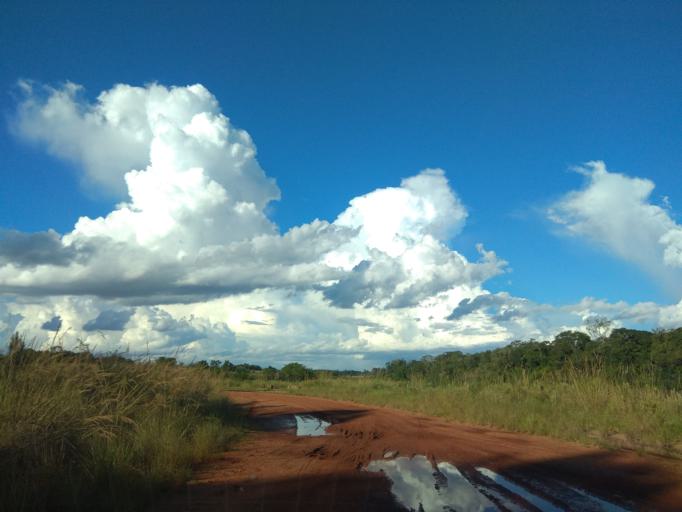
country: AR
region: Misiones
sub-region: Departamento de Candelaria
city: Candelaria
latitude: -27.4920
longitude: -55.7590
